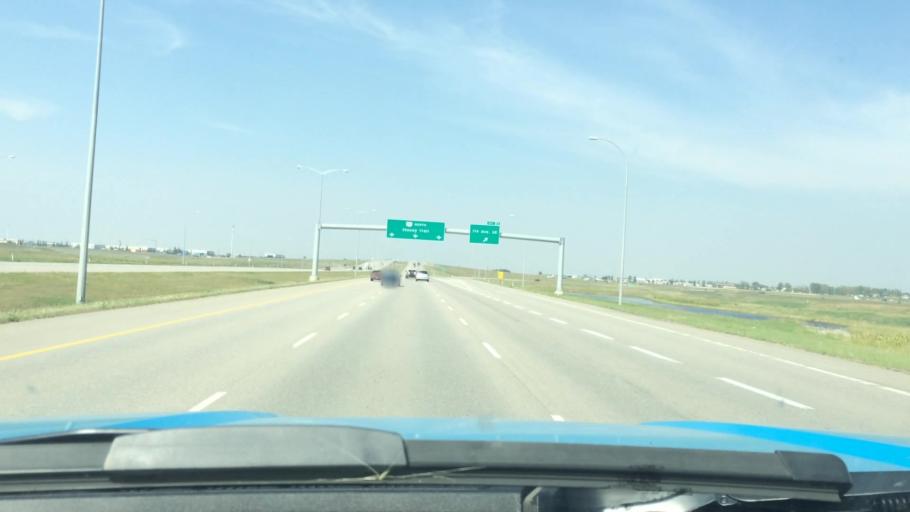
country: CA
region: Alberta
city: Chestermere
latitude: 50.9384
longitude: -113.9200
